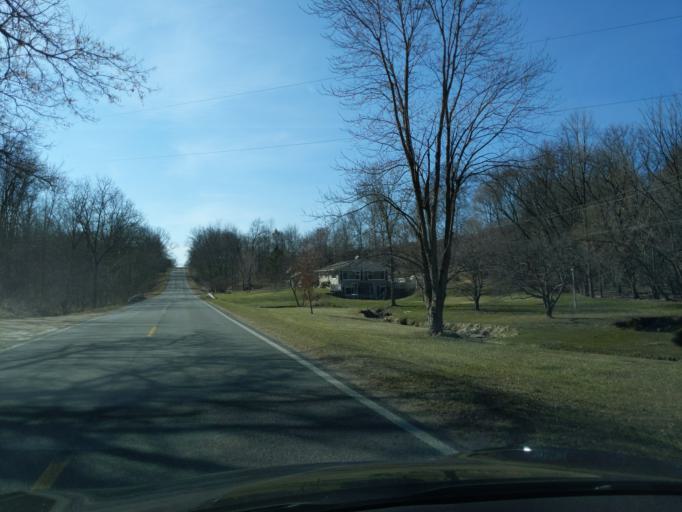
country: US
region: Michigan
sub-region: Ionia County
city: Saranac
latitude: 42.9296
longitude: -85.1672
